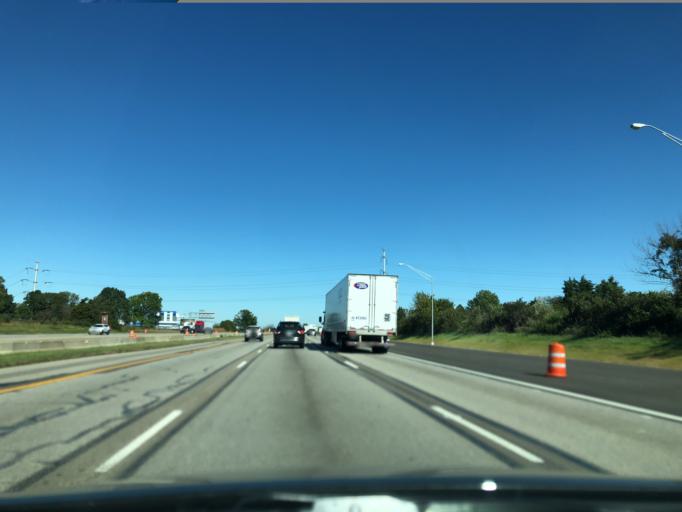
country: US
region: Ohio
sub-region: Warren County
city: Landen
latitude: 39.3403
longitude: -84.2798
